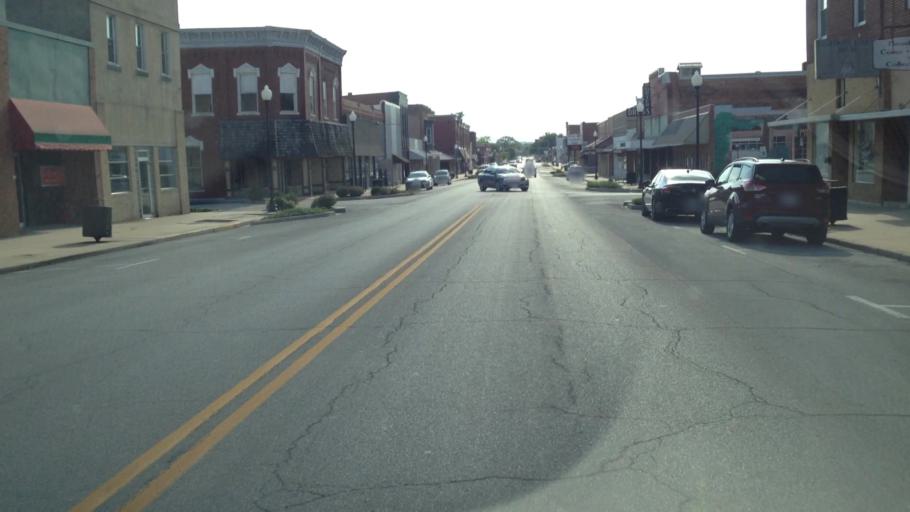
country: US
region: Kansas
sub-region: Wilson County
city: Neodesha
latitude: 37.4175
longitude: -95.6793
